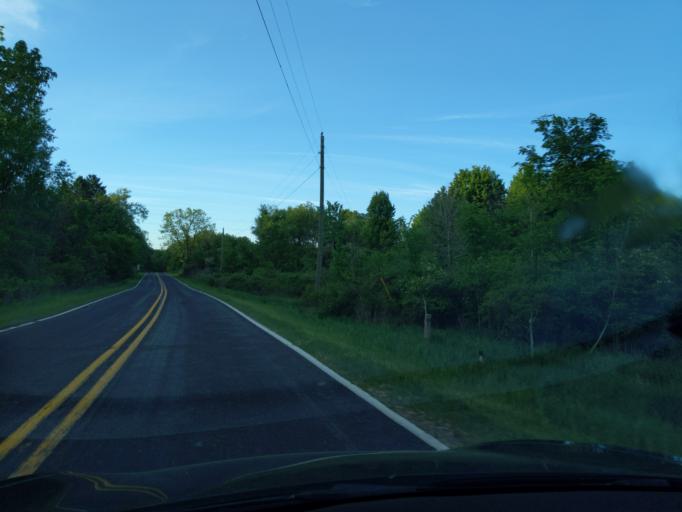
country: US
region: Michigan
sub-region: Ingham County
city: Leslie
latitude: 42.4979
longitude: -84.3148
